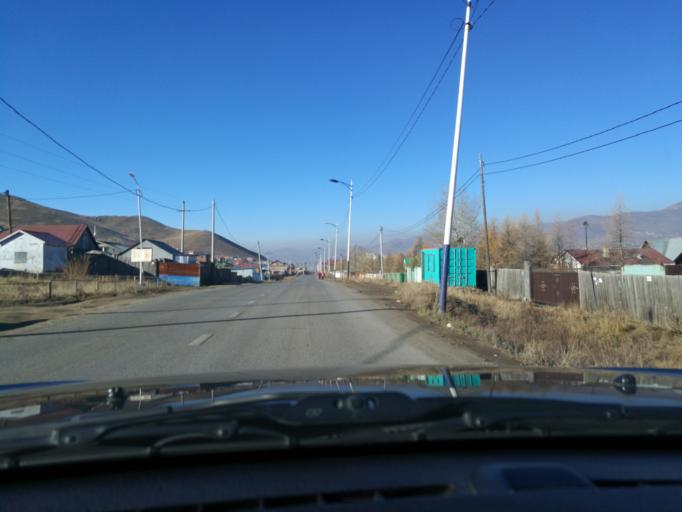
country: MN
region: Ulaanbaatar
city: Ulaanbaatar
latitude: 47.9808
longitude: 106.9490
